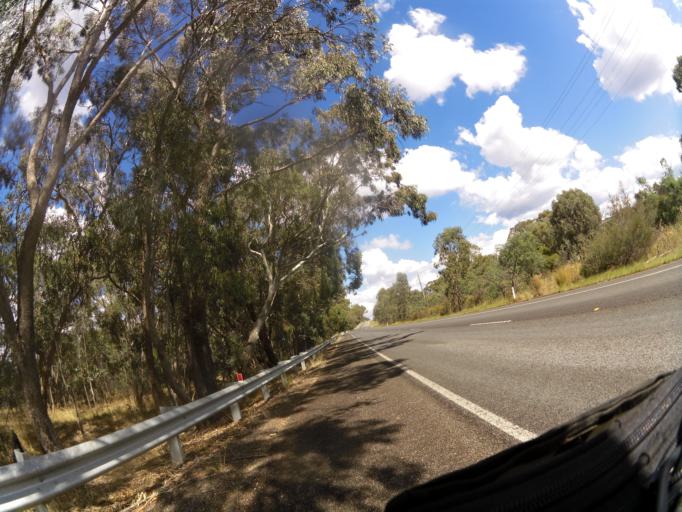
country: AU
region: Victoria
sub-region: Benalla
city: Benalla
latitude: -36.7876
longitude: 146.0106
